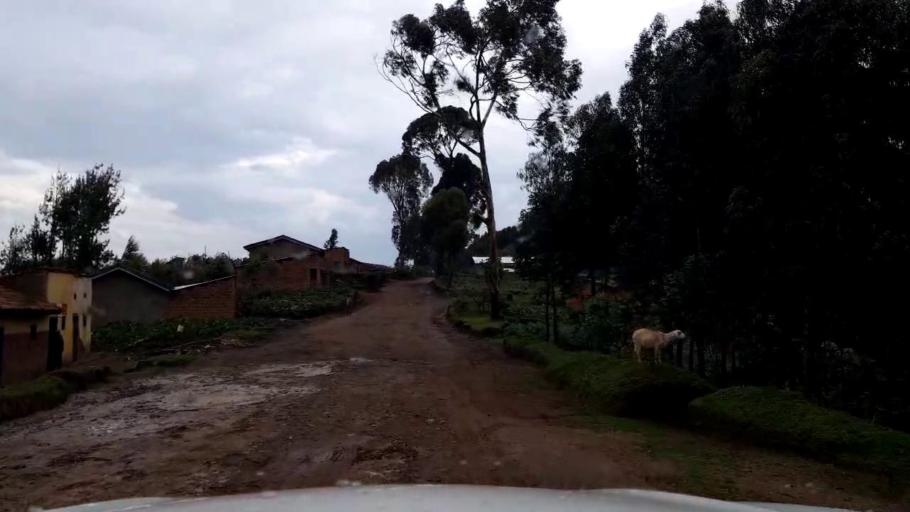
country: RW
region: Western Province
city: Kibuye
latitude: -2.0244
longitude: 29.4557
